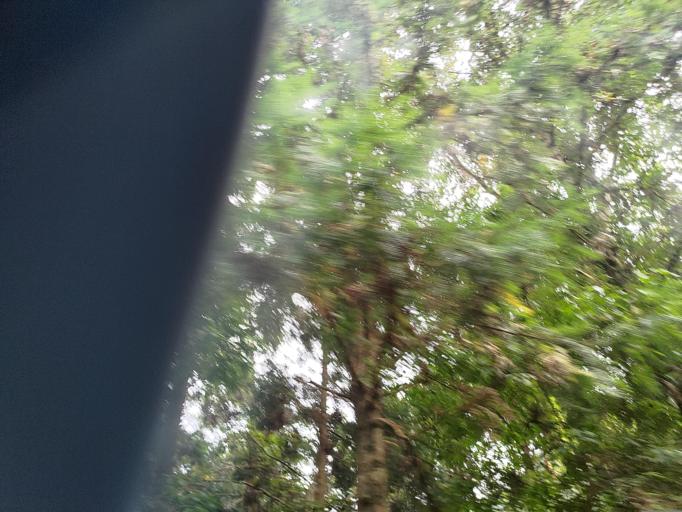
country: TW
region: Taiwan
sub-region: Hsinchu
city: Hsinchu
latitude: 24.6266
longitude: 121.0610
